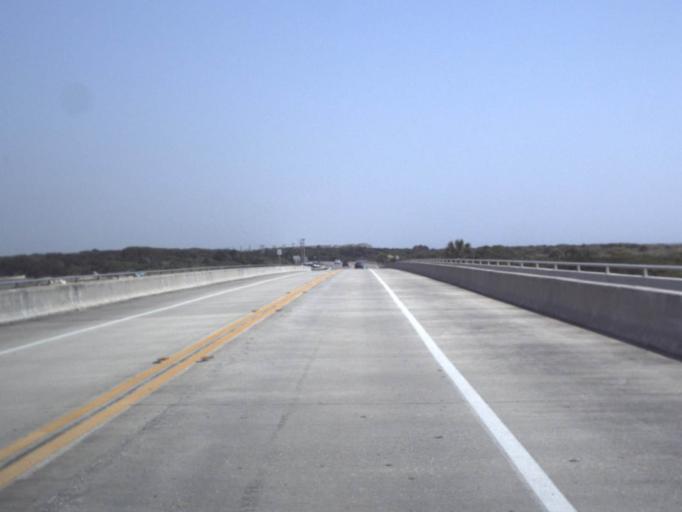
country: US
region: Florida
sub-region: Saint Johns County
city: Butler Beach
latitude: 29.7081
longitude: -81.2288
